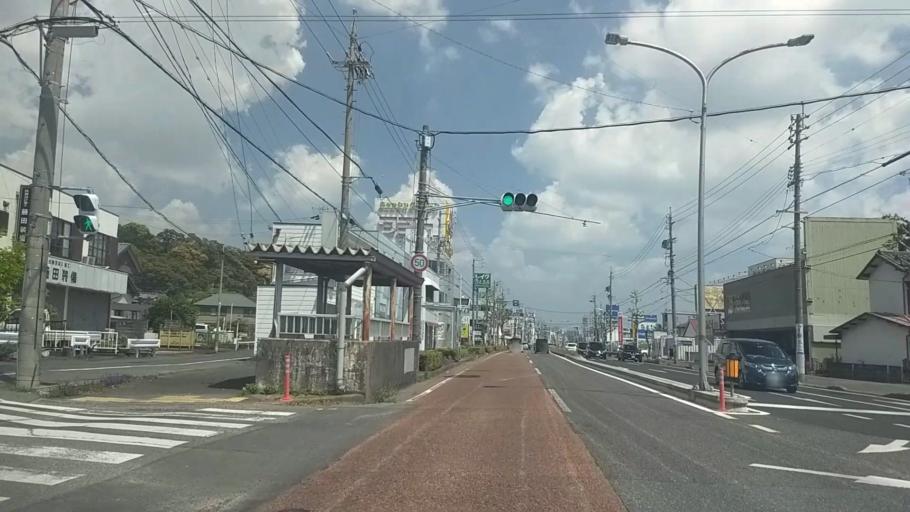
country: JP
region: Shizuoka
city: Hamamatsu
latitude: 34.7252
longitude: 137.7311
